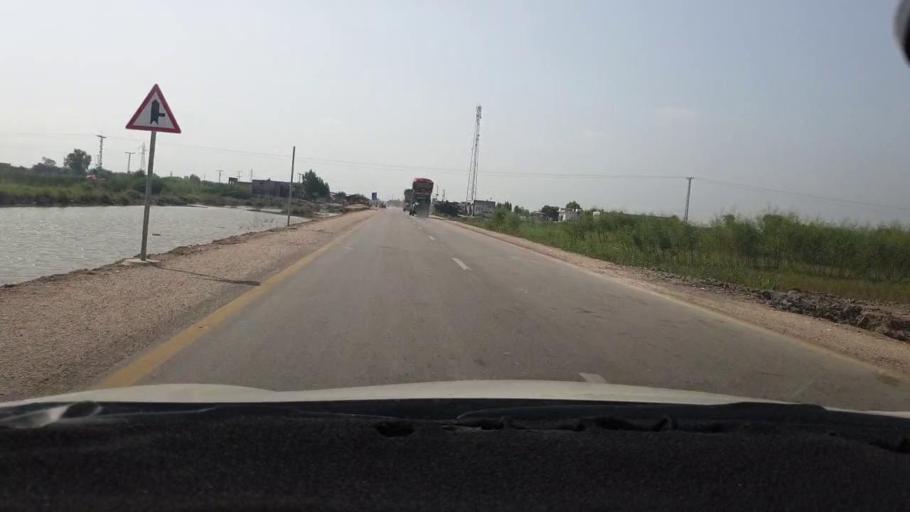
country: PK
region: Sindh
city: Tando Mittha Khan
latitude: 25.8290
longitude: 69.0642
